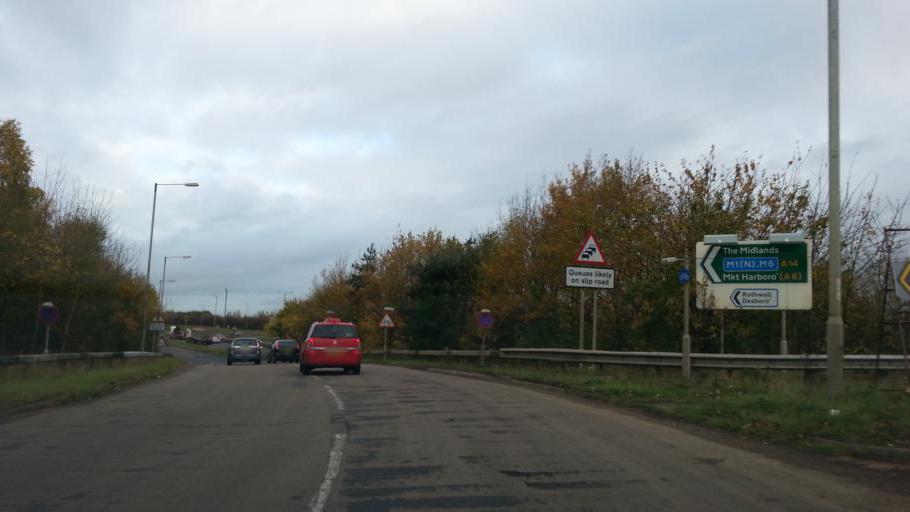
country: GB
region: England
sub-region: Northamptonshire
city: Kettering
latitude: 52.4077
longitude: -0.7549
